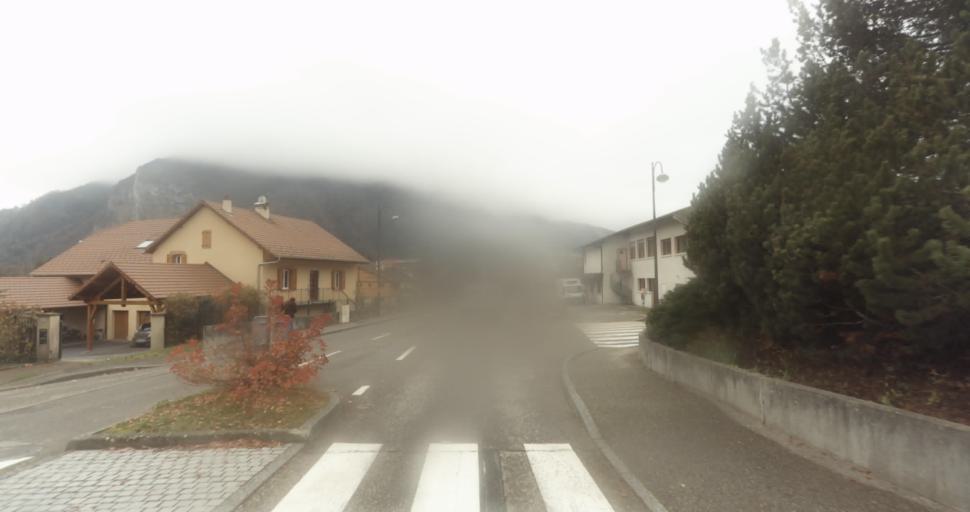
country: FR
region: Rhone-Alpes
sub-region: Departement de la Haute-Savoie
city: Thorens-Glieres
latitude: 45.9982
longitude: 6.2503
